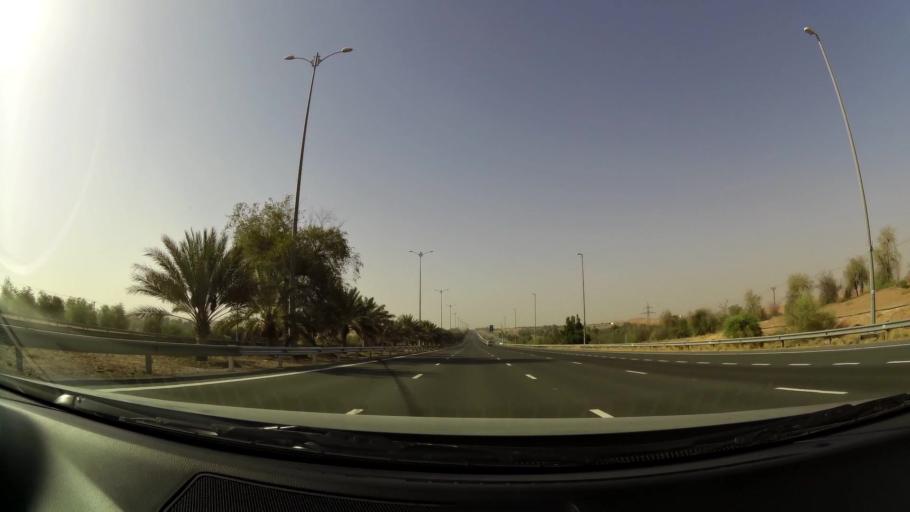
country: OM
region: Al Buraimi
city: Al Buraymi
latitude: 24.5546
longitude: 55.7537
